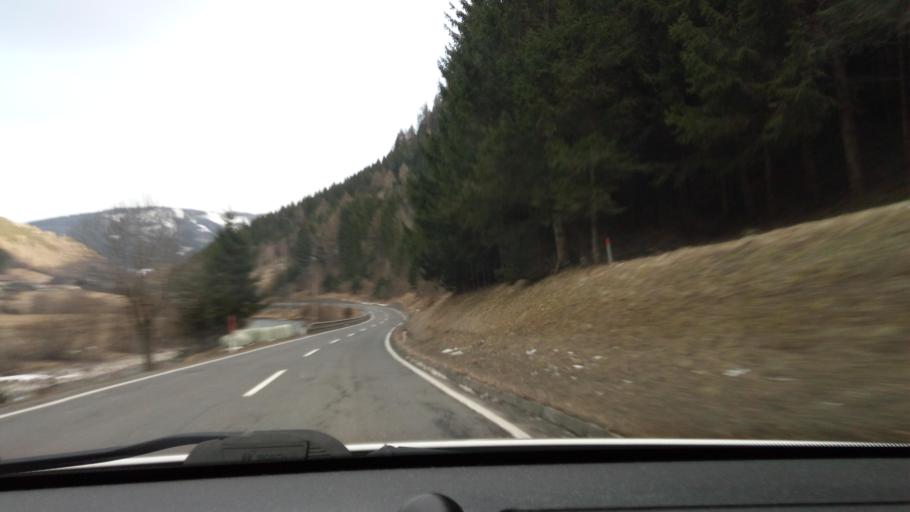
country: AT
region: Salzburg
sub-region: Politischer Bezirk Tamsweg
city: Ramingstein
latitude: 47.0743
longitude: 13.8520
